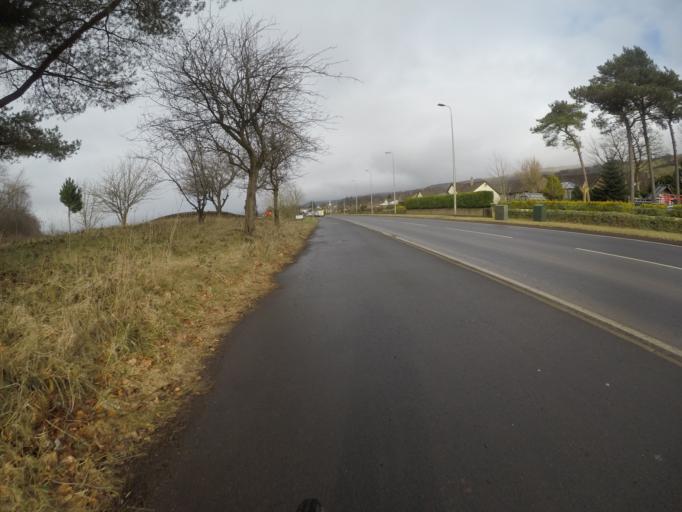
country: GB
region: Scotland
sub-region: North Ayrshire
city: Fairlie
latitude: 55.7467
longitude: -4.8572
